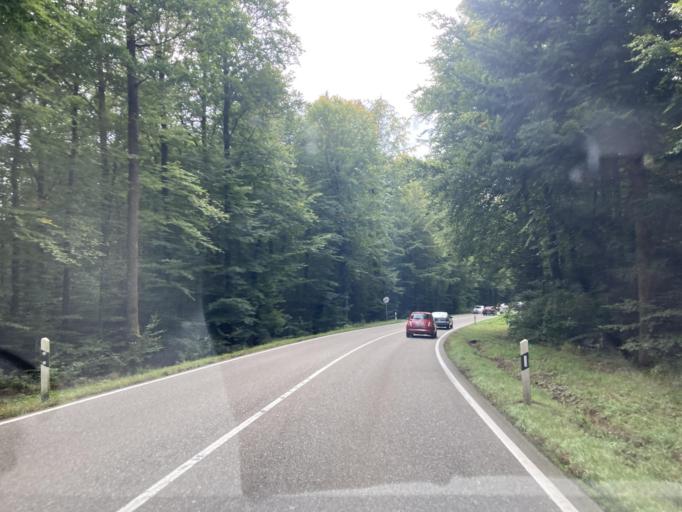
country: DE
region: Baden-Wuerttemberg
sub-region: Karlsruhe Region
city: Neuenburg
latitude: 48.8582
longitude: 8.6083
